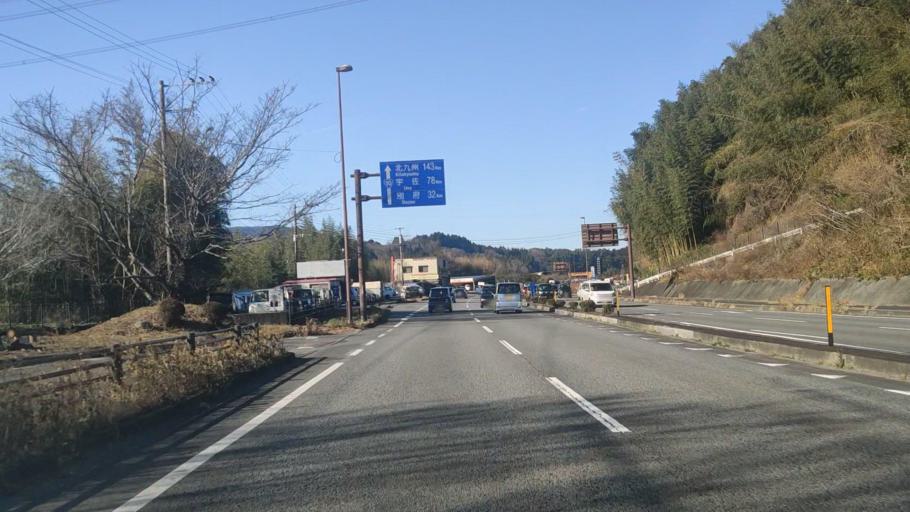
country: JP
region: Oita
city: Oita
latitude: 33.1135
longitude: 131.6554
